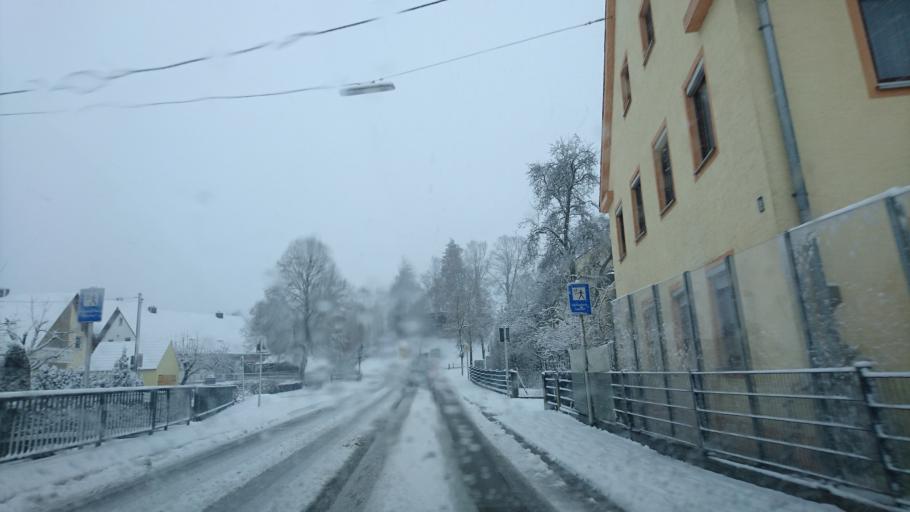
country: DE
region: Bavaria
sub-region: Swabia
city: Emersacker
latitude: 48.4898
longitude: 10.6730
